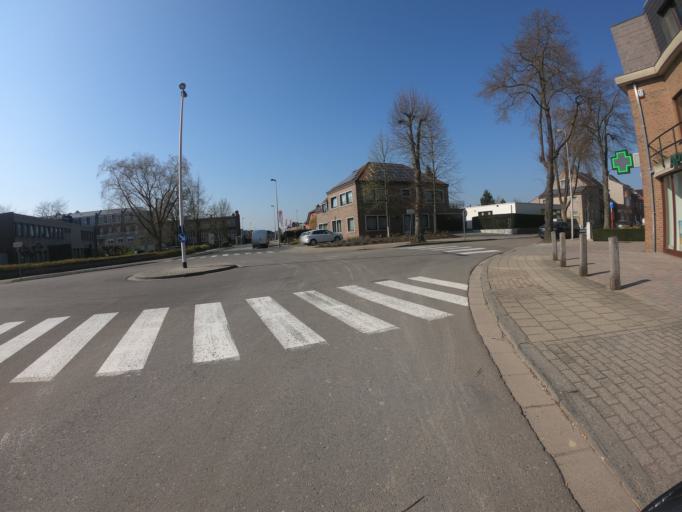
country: BE
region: Flanders
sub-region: Provincie Limburg
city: Sint-Truiden
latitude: 50.8211
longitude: 5.1801
